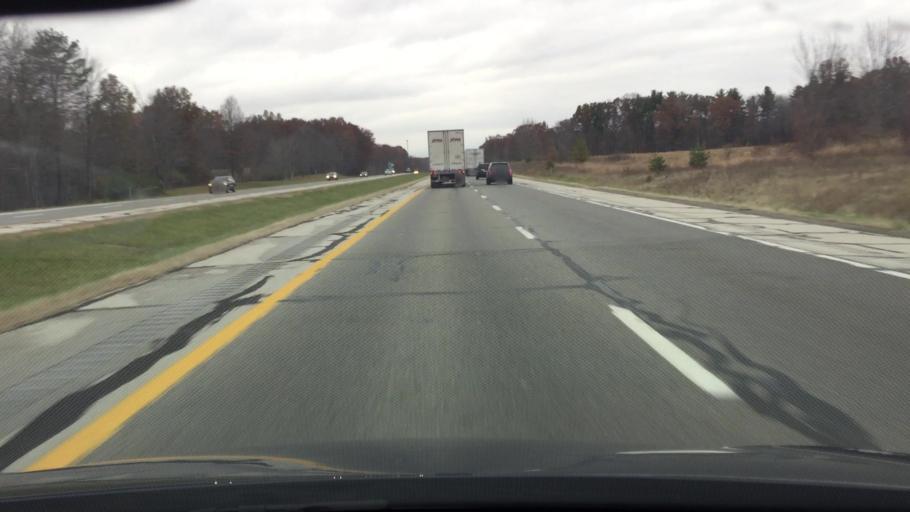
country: US
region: Ohio
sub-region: Mahoning County
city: Canfield
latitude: 41.0458
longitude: -80.7651
